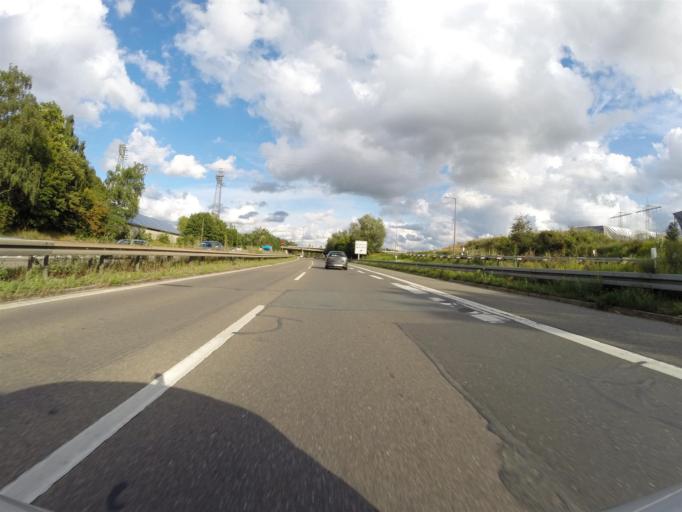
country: DE
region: Bavaria
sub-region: Regierungsbezirk Mittelfranken
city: Nuernberg
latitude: 49.4147
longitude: 11.0610
